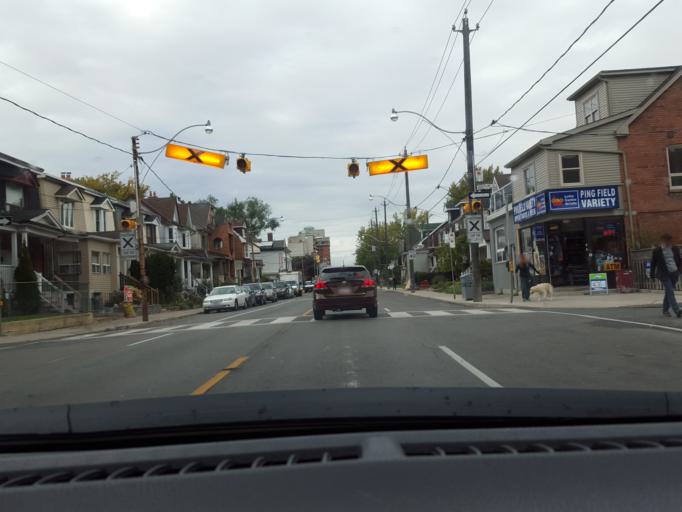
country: CA
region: Ontario
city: Toronto
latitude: 43.6757
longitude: -79.3435
